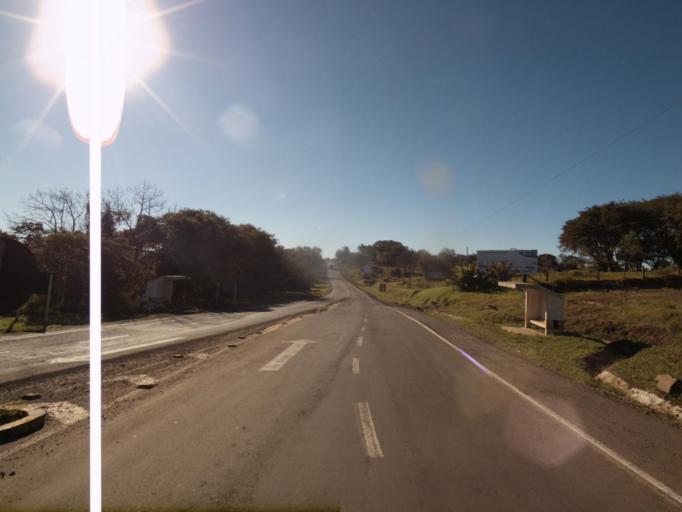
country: AR
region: Misiones
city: Bernardo de Irigoyen
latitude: -26.6555
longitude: -53.5172
